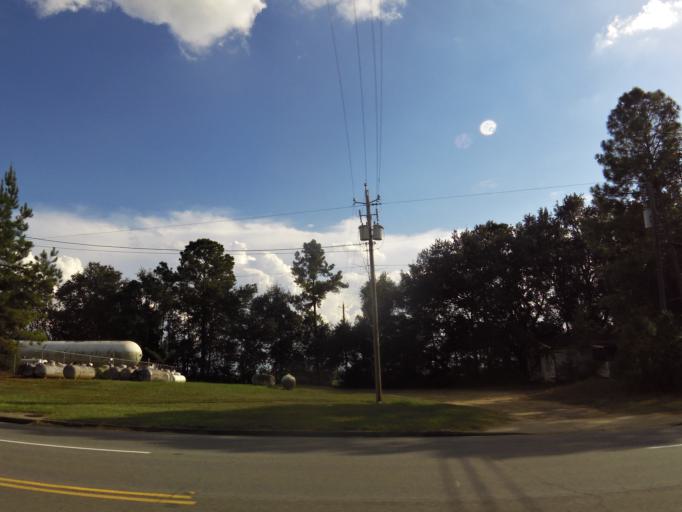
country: US
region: Georgia
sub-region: Brooks County
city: Quitman
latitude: 30.7858
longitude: -83.5843
